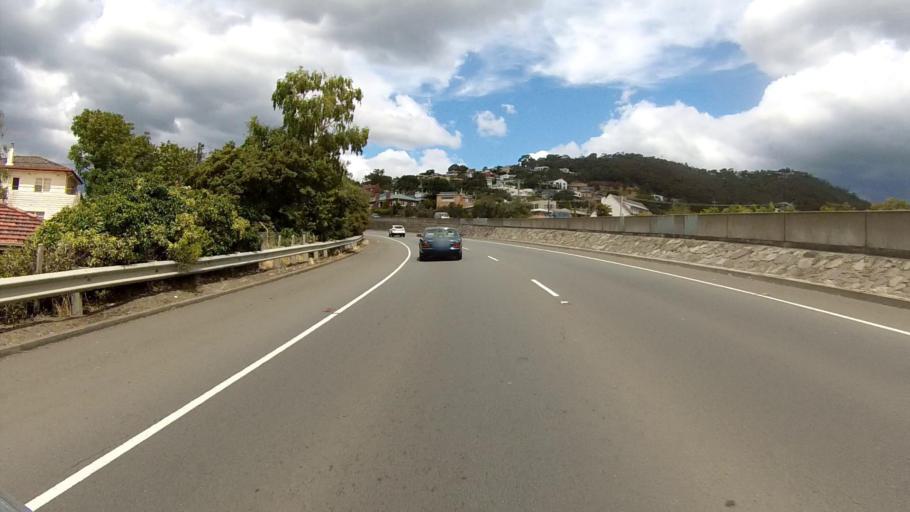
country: AU
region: Tasmania
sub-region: Hobart
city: Dynnyrne
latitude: -42.8992
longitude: 147.3156
